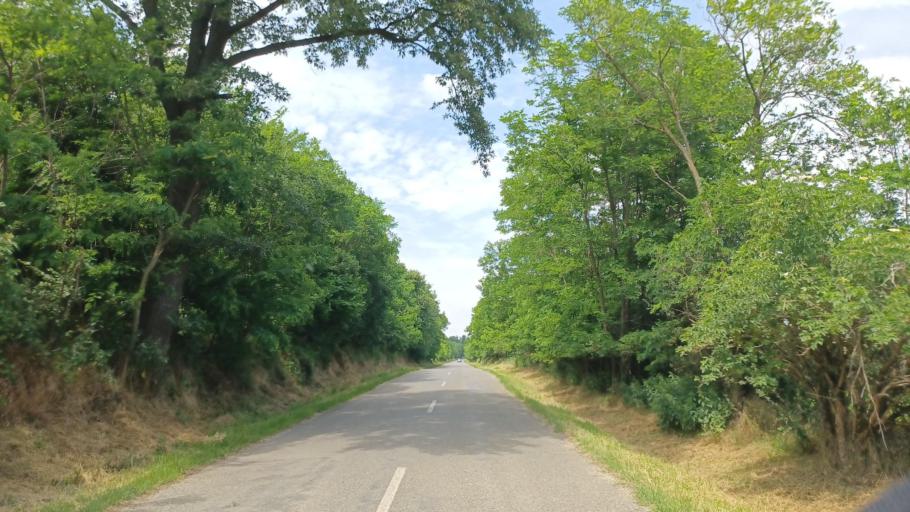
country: HU
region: Tolna
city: Simontornya
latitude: 46.7038
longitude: 18.5130
